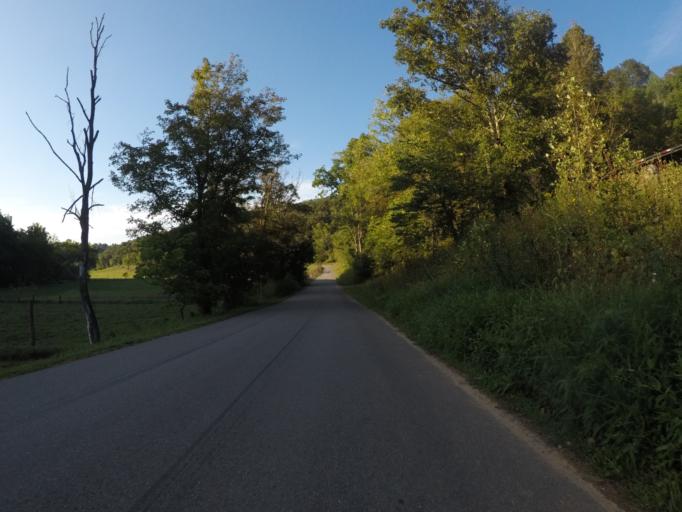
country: US
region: Ohio
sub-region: Lawrence County
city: Coal Grove
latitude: 38.5443
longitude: -82.5505
